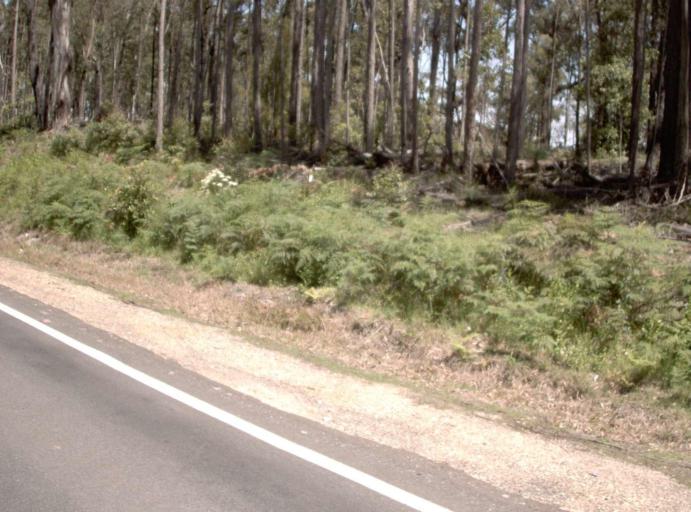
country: AU
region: New South Wales
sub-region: Bombala
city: Bombala
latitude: -37.5872
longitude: 148.9541
